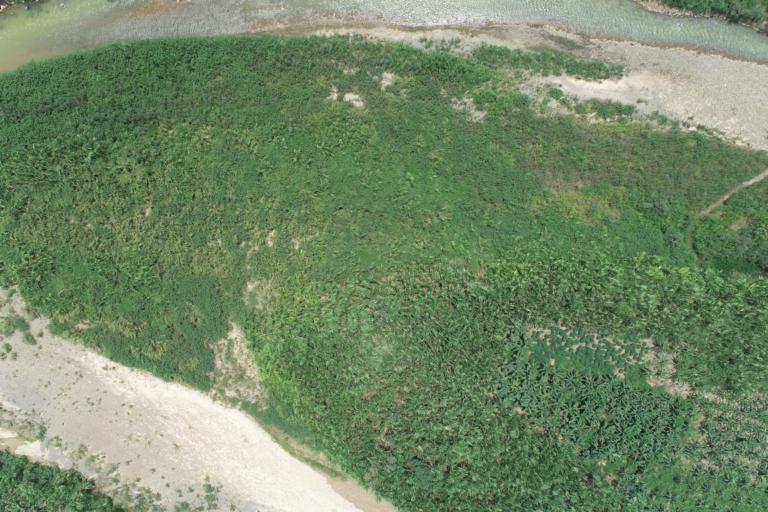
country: BO
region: La Paz
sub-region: Provincia Larecaja
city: Guanay
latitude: -15.7682
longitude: -67.6647
